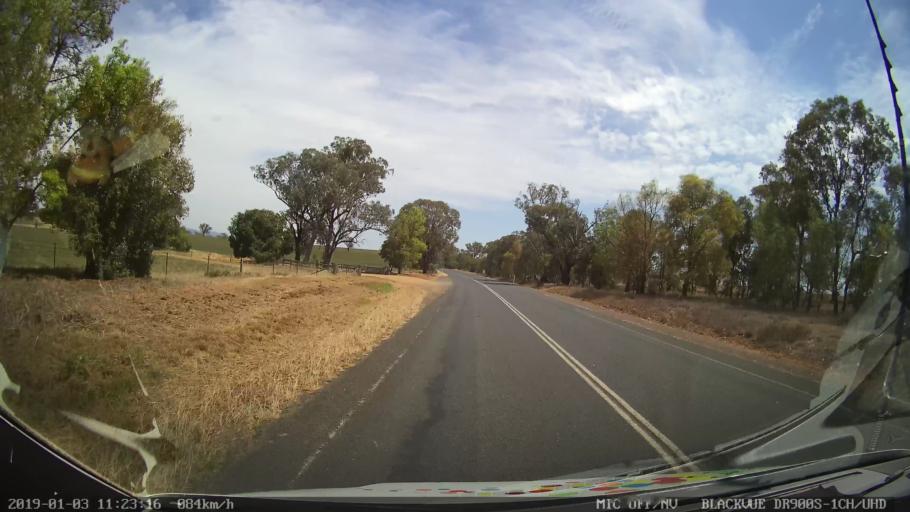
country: AU
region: New South Wales
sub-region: Weddin
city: Grenfell
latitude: -34.0651
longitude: 148.2436
